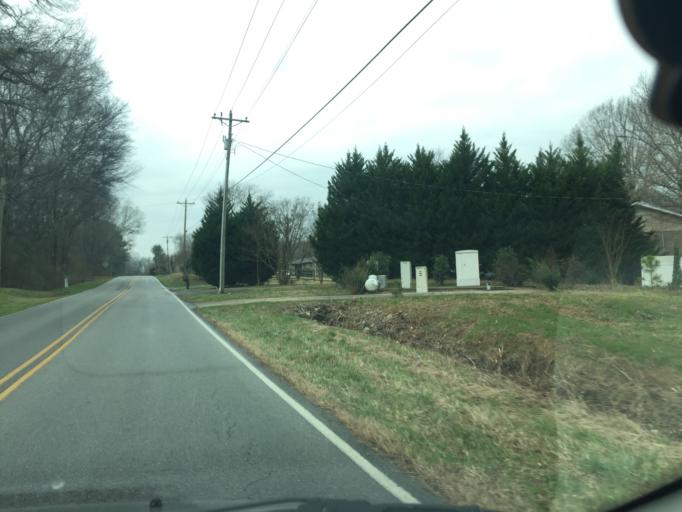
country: US
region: Tennessee
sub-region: Hamilton County
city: East Brainerd
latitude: 34.9755
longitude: -85.1485
